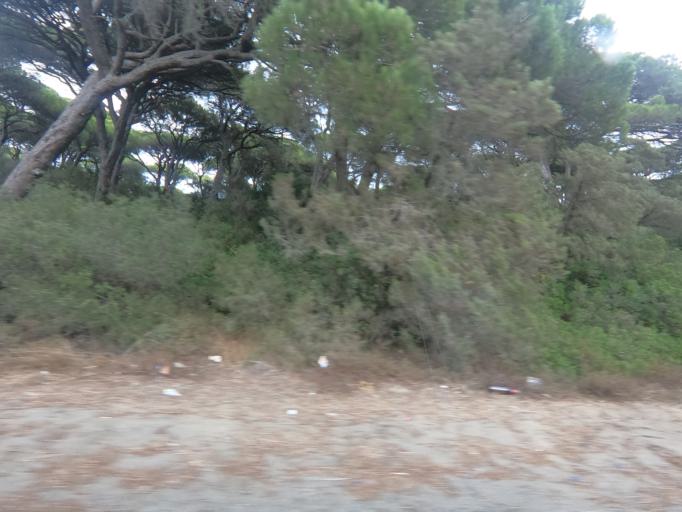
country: PT
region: Setubal
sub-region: Almada
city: Charneca
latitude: 38.6025
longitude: -9.1962
